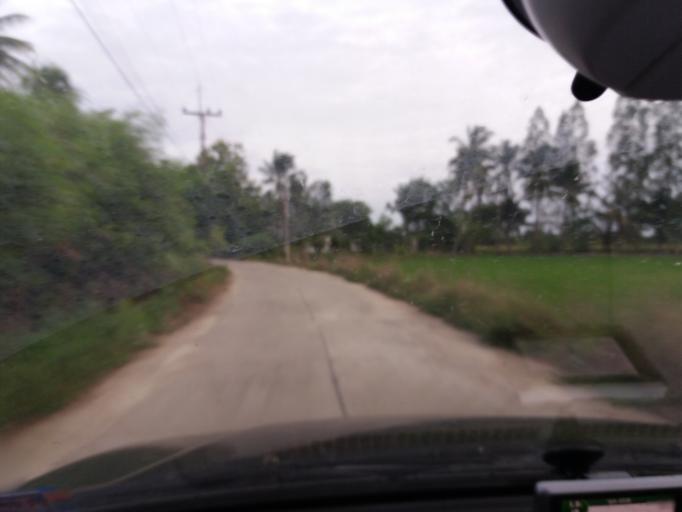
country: TH
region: Suphan Buri
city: Ban Sam Chuk
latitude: 14.7154
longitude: 100.0468
